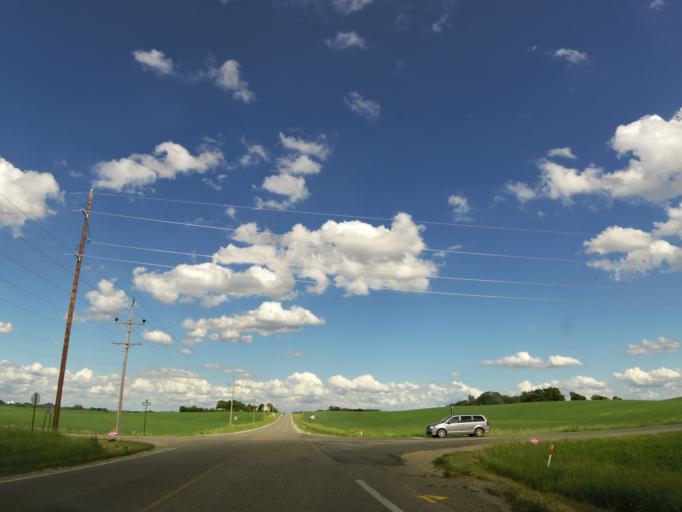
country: US
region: Minnesota
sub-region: Meeker County
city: Dassel
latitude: 45.0664
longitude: -94.2774
